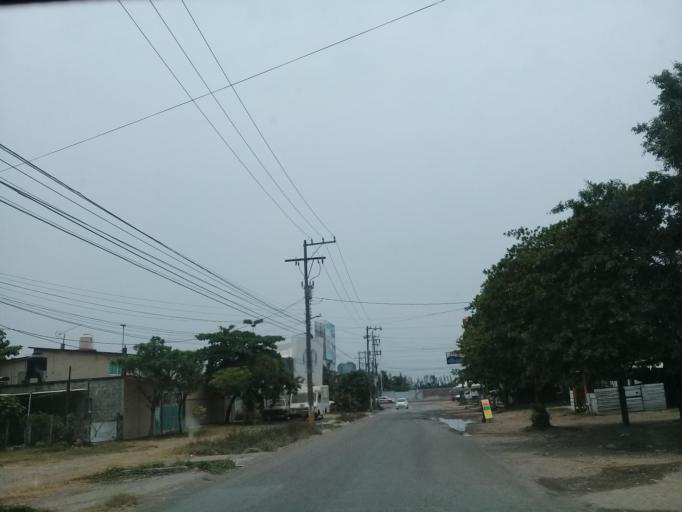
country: MX
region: Veracruz
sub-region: Veracruz
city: Las Amapolas
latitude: 19.1613
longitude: -96.2083
